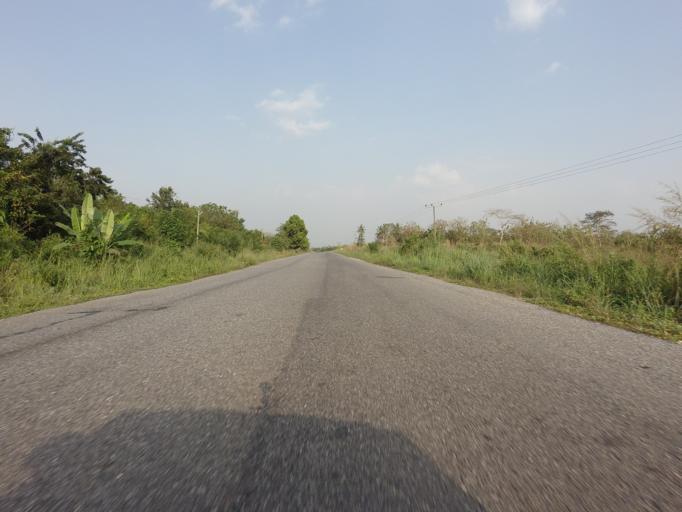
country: GH
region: Volta
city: Ho
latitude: 6.4195
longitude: 0.1813
